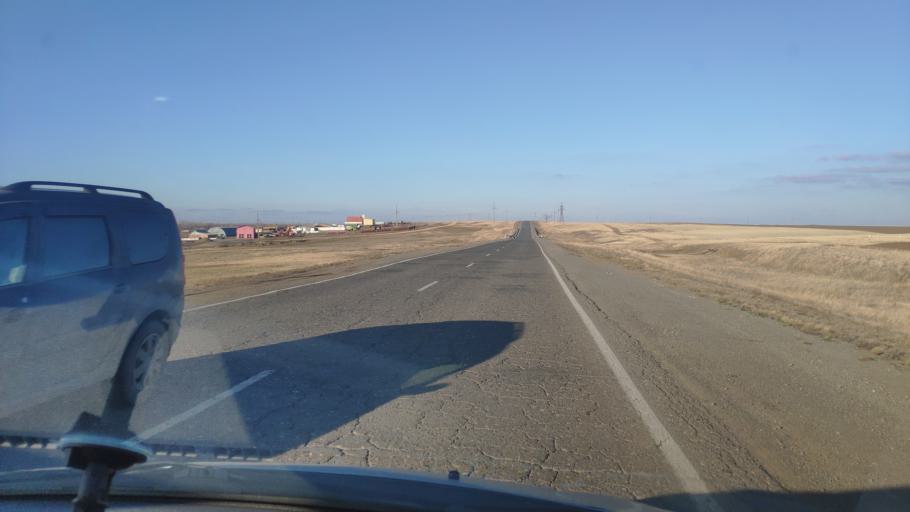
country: RU
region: Orenburg
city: Gay
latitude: 51.6311
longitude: 58.3647
